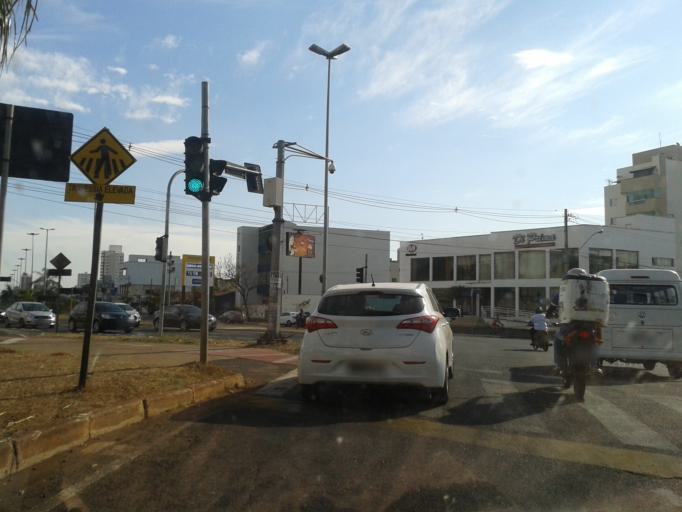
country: BR
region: Minas Gerais
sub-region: Uberlandia
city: Uberlandia
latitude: -18.9139
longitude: -48.2617
